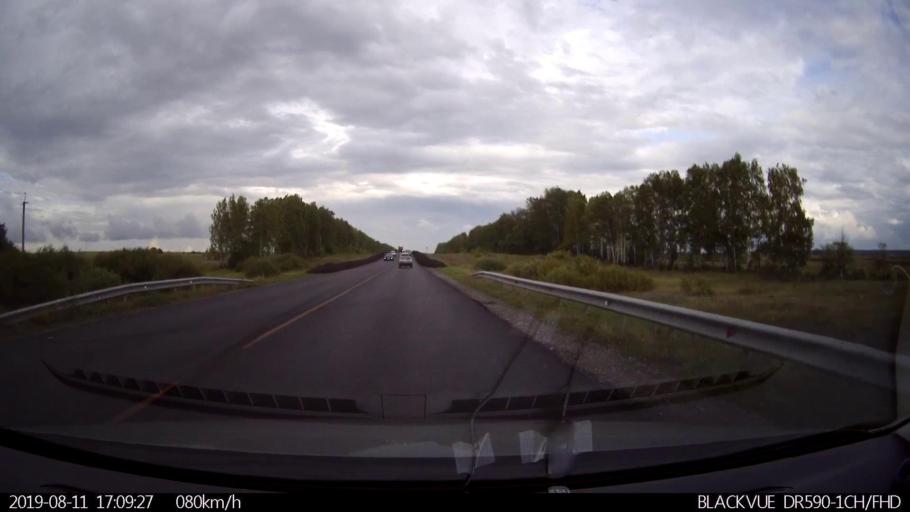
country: RU
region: Ulyanovsk
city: Mayna
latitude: 54.2958
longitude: 47.8566
